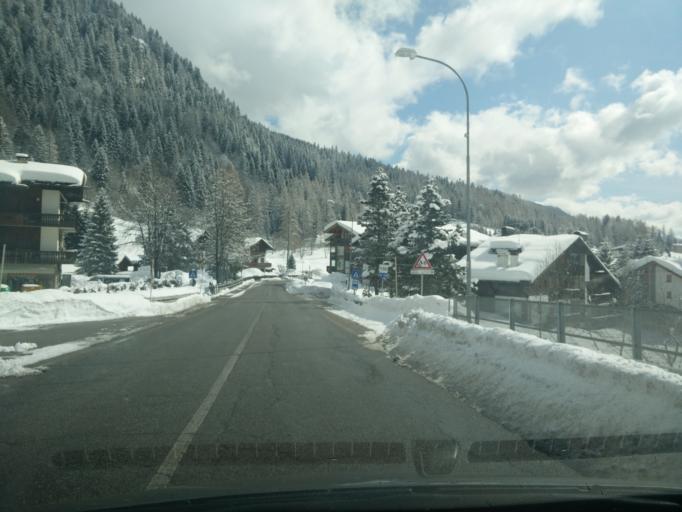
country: IT
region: Veneto
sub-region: Provincia di Belluno
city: Fusine
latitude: 46.3915
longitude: 12.1076
